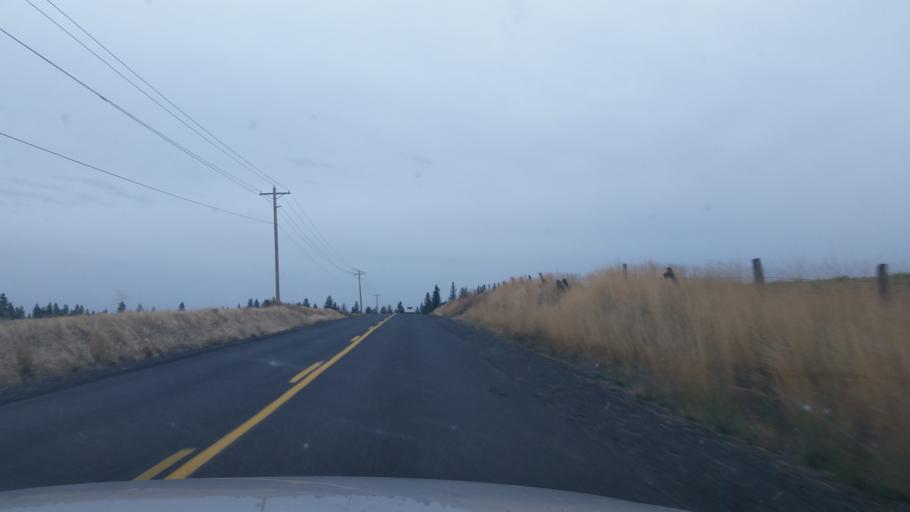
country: US
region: Washington
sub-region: Spokane County
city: Cheney
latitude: 47.5131
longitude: -117.5506
